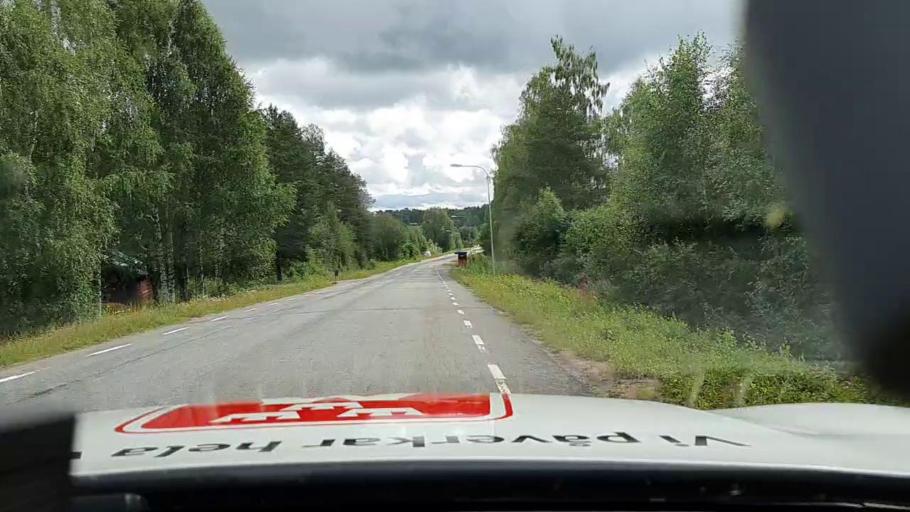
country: SE
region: Norrbotten
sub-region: Overkalix Kommun
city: OEverkalix
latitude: 66.2581
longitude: 22.8169
